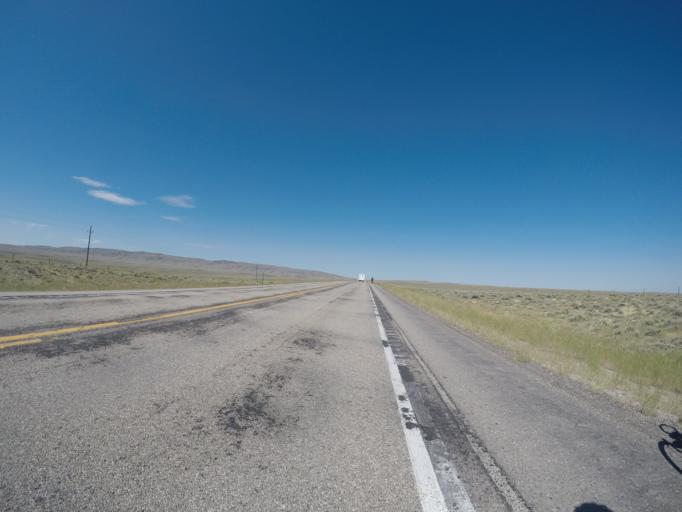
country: US
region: Wyoming
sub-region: Carbon County
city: Saratoga
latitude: 41.8171
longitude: -106.6646
